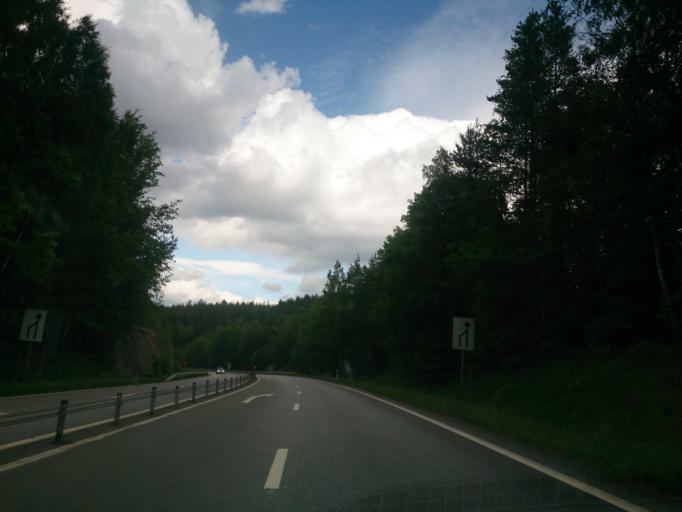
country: SE
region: OEstergoetland
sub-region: Norrkopings Kommun
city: Jursla
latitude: 58.6901
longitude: 16.1557
